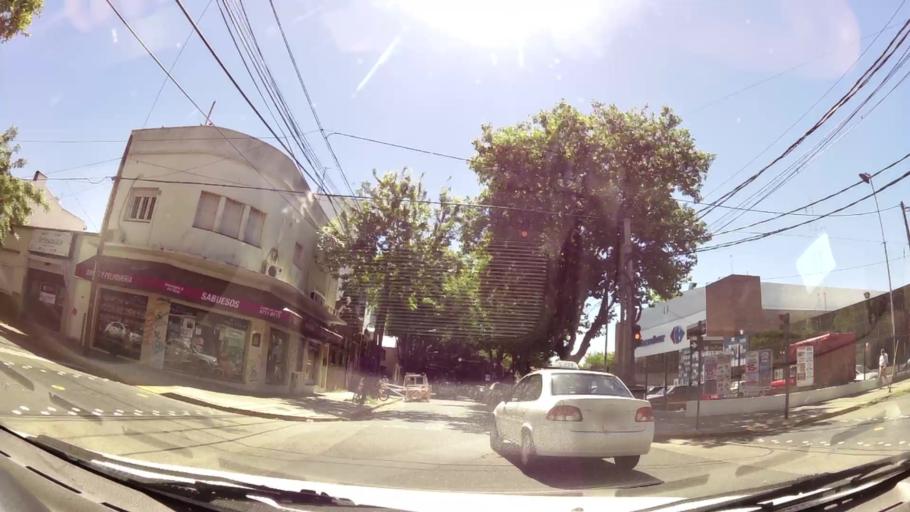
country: AR
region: Buenos Aires
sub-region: Partido de Vicente Lopez
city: Olivos
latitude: -34.5160
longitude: -58.4955
